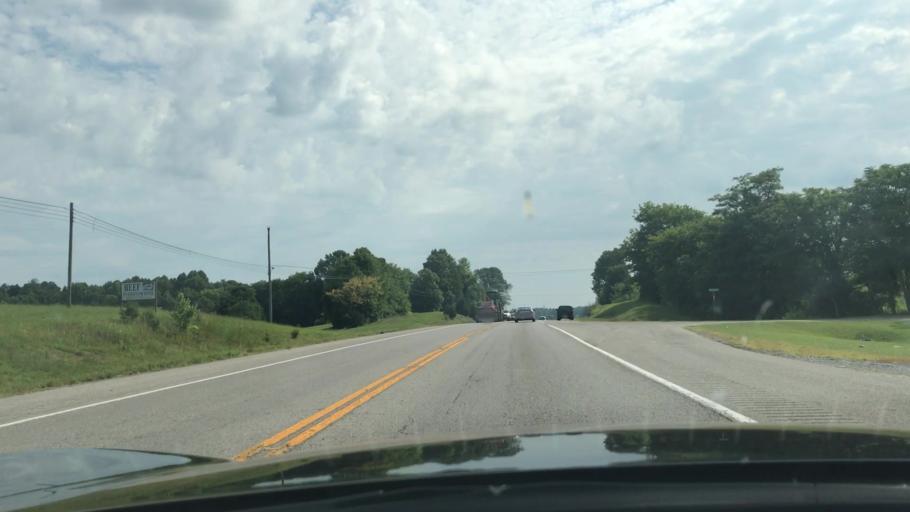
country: US
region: Kentucky
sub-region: Green County
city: Greensburg
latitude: 37.2884
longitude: -85.4794
